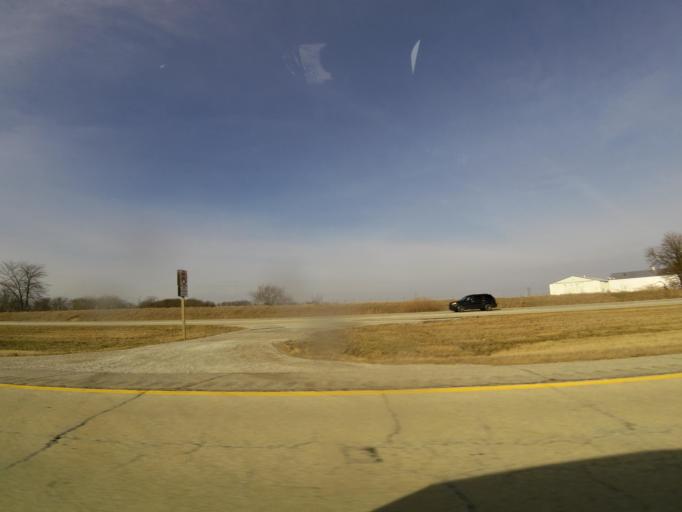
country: US
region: Illinois
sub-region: Macon County
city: Warrensburg
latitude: 39.8889
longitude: -89.0140
